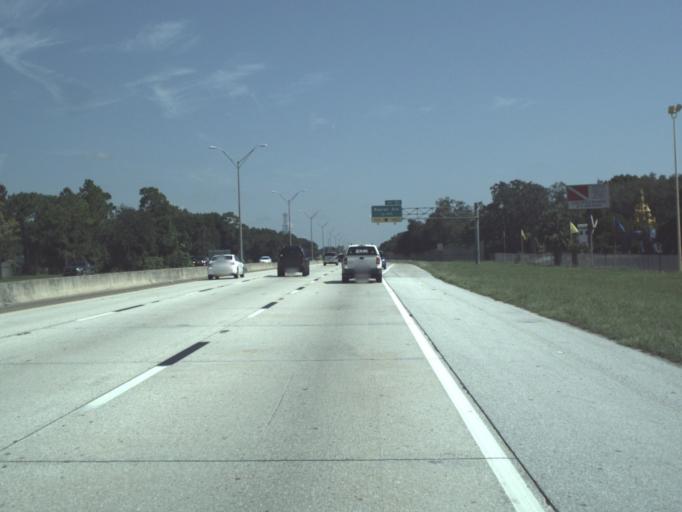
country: US
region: Florida
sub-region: Hillsborough County
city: Lake Magdalene
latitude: 28.0766
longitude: -82.4546
